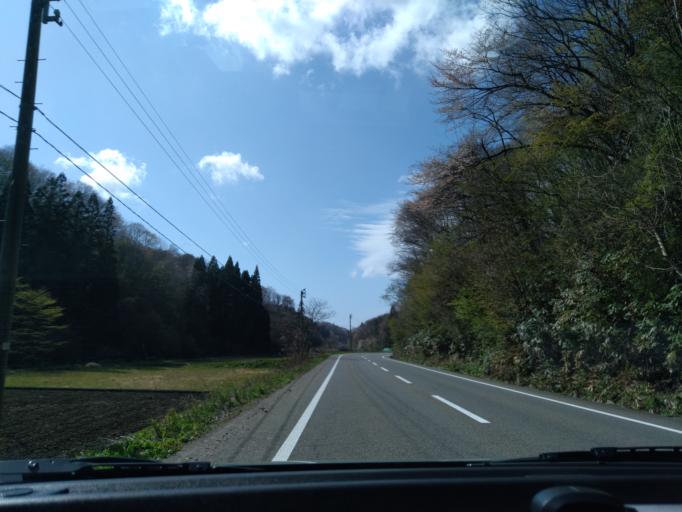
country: JP
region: Akita
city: Akita
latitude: 39.7032
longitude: 140.2154
